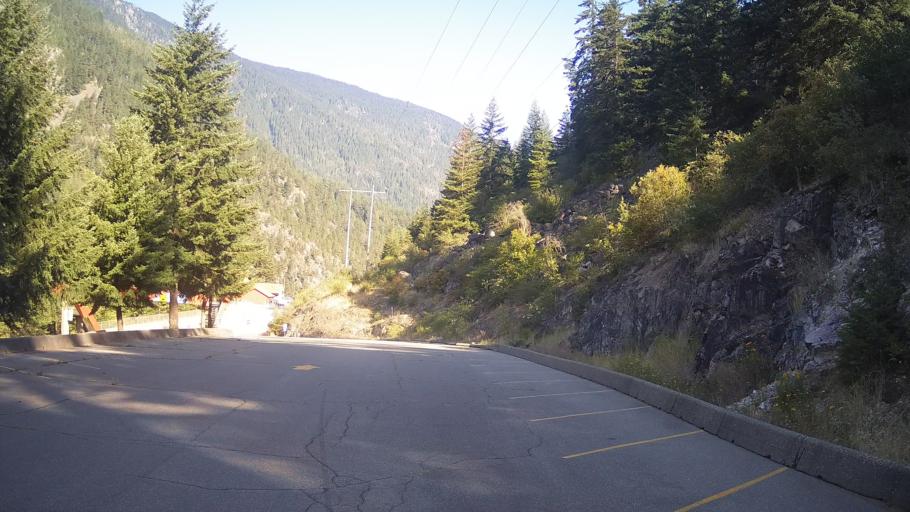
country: CA
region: British Columbia
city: Hope
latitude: 49.7803
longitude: -121.4440
